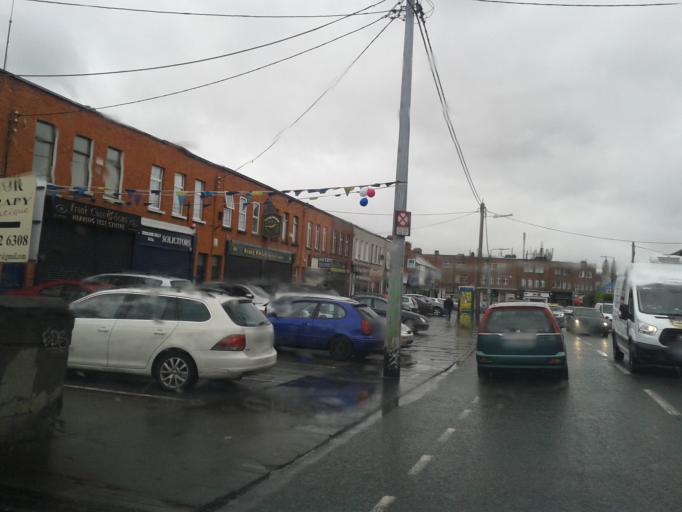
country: IE
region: Leinster
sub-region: South Dublin
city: Terenure
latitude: 53.3186
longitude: -6.2916
